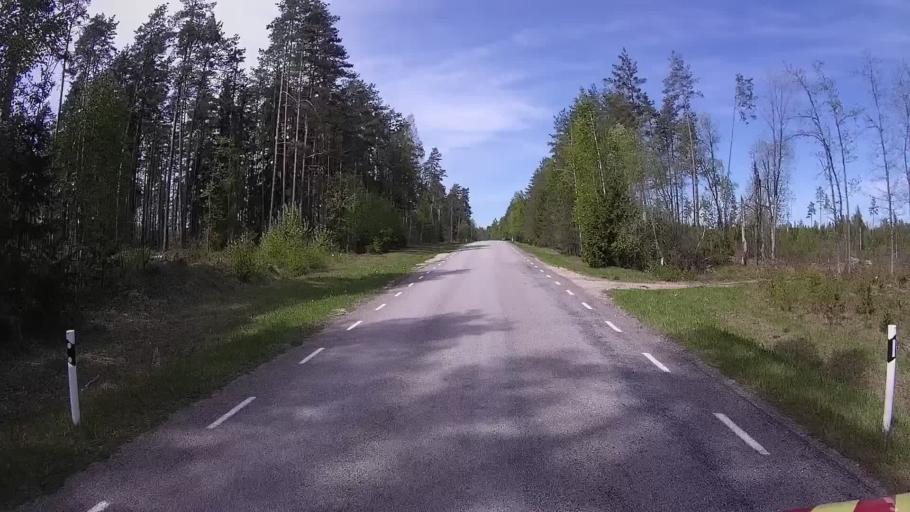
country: EE
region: Vorumaa
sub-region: Antsla vald
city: Vana-Antsla
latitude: 57.6180
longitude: 26.3557
